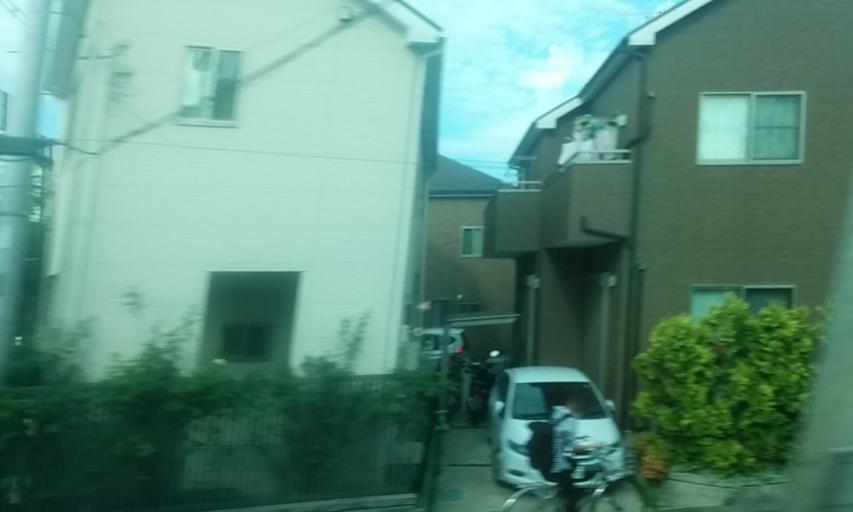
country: JP
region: Saitama
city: Yono
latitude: 35.8737
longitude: 139.6441
